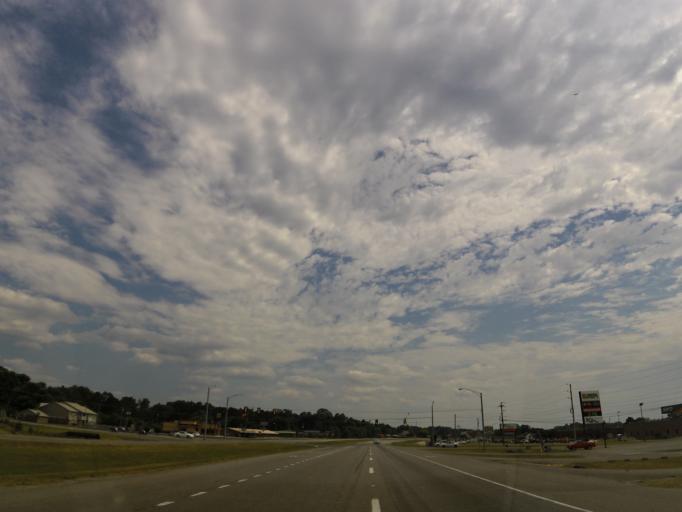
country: US
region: Alabama
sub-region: Jackson County
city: Stevenson
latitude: 34.8742
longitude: -85.8128
